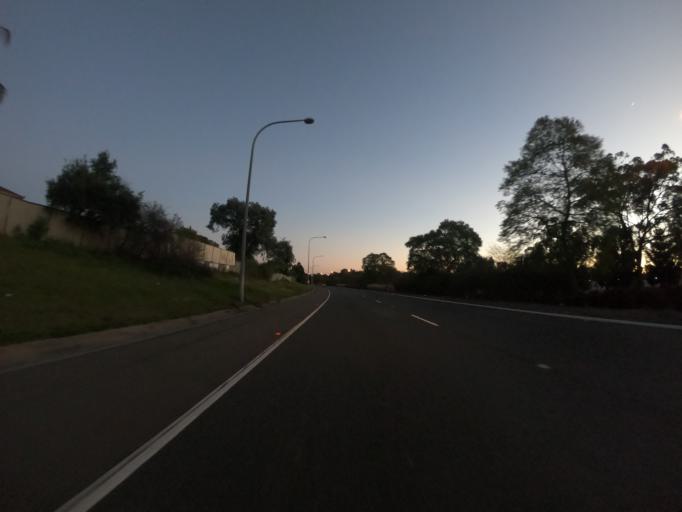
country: AU
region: New South Wales
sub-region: Campbelltown Municipality
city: Leumeah
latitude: -34.0416
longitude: 150.8290
